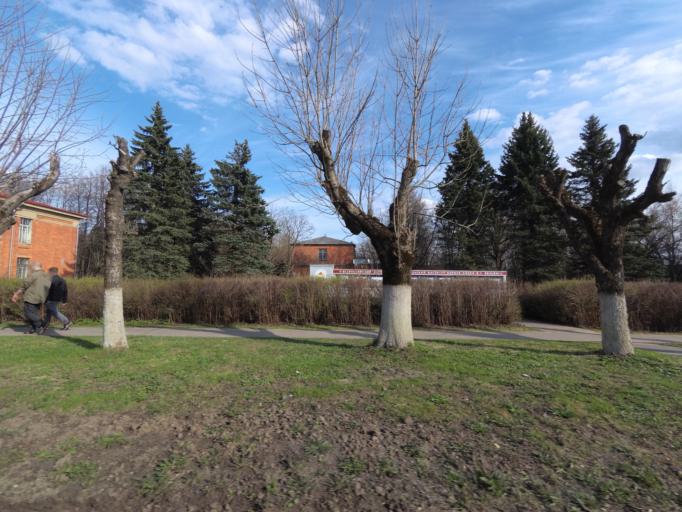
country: RU
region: Moskovskaya
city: Lugovaya
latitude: 56.0434
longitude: 37.4805
